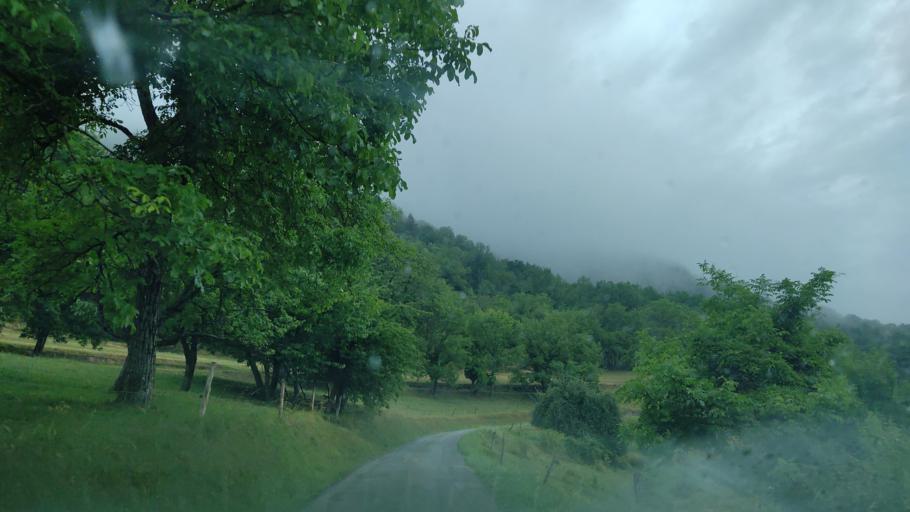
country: FR
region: Rhone-Alpes
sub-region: Departement de la Savoie
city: Coise-Saint-Jean-Pied-Gauthier
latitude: 45.4987
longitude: 6.1468
